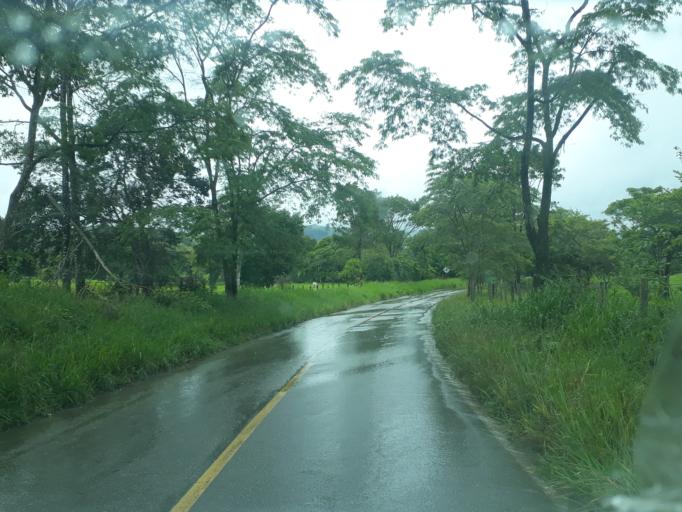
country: CO
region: Cundinamarca
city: Medina
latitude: 4.4583
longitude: -73.3266
